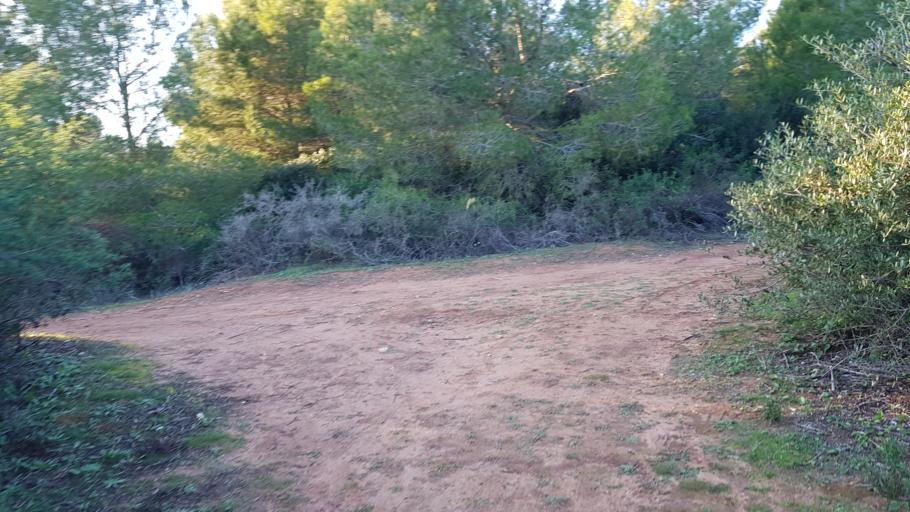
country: IT
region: Apulia
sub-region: Provincia di Lecce
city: Nardo
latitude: 40.1525
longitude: 17.9637
